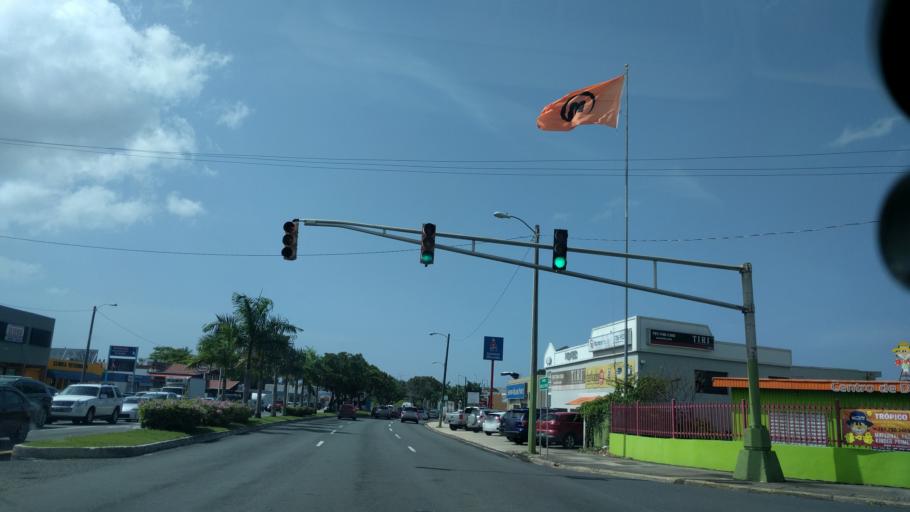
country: PR
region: Bayamon
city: Bayamon
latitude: 18.4179
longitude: -66.1633
